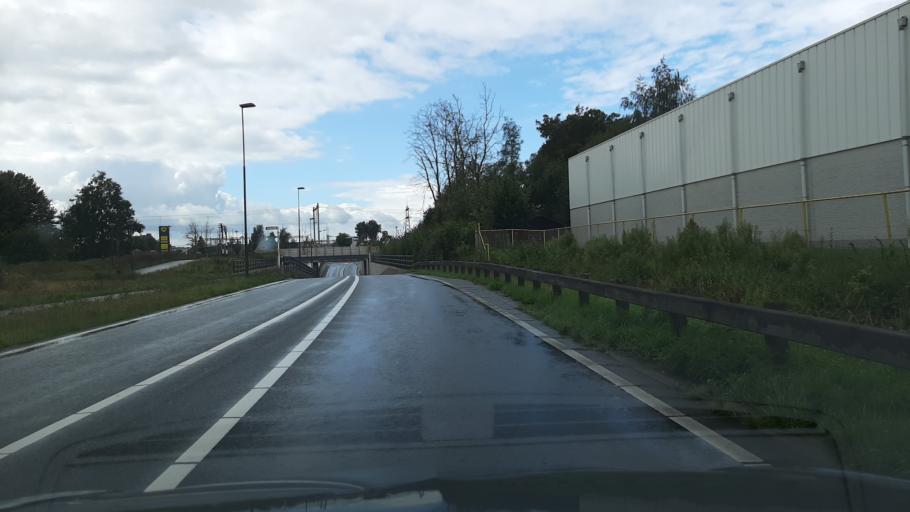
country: NL
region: Friesland
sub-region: Gemeente Weststellingwerf
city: Wolvega
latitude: 52.8839
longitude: 6.0027
